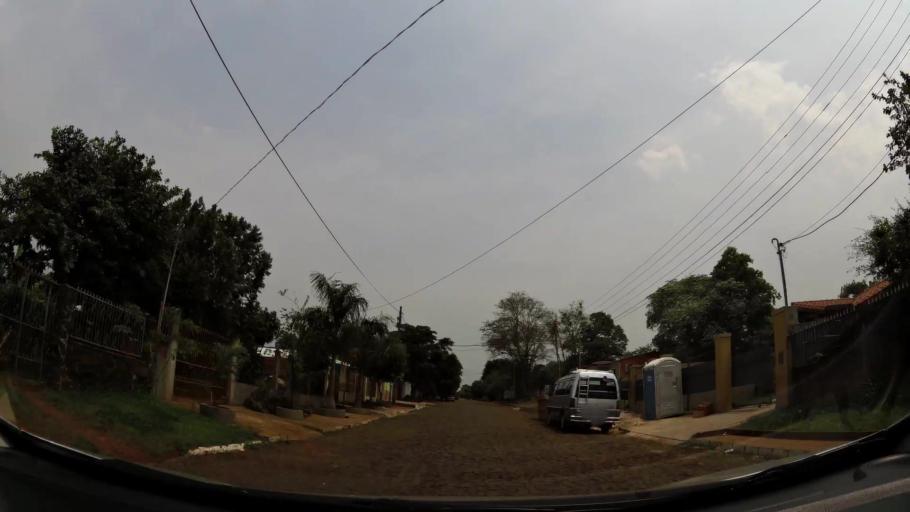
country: BR
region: Parana
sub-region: Foz Do Iguacu
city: Foz do Iguacu
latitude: -25.5689
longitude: -54.6077
